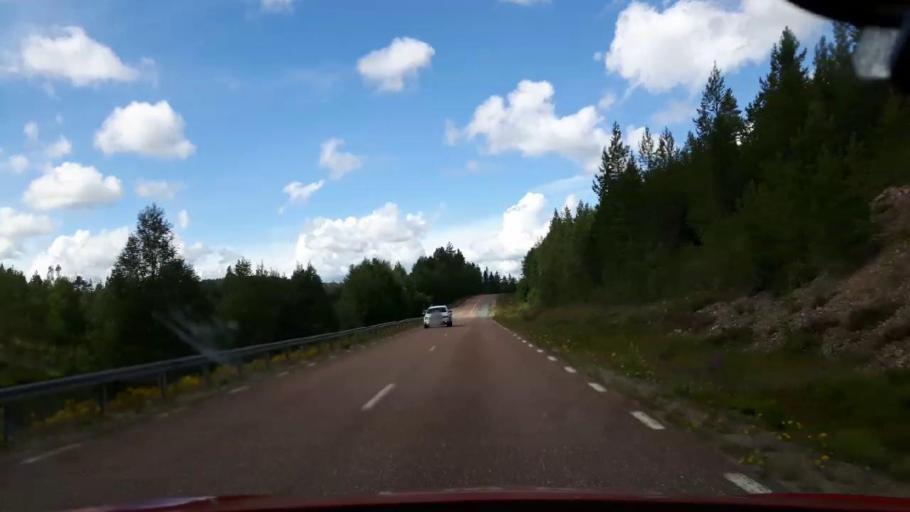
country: SE
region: Dalarna
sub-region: Alvdalens Kommun
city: AElvdalen
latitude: 61.7981
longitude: 13.6895
